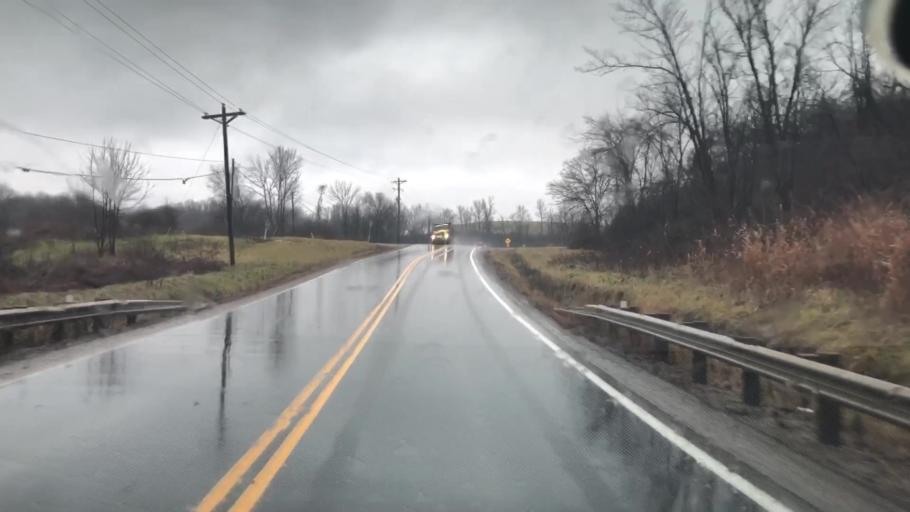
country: US
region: Ohio
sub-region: Harrison County
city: Cadiz
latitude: 40.2212
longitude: -81.0014
